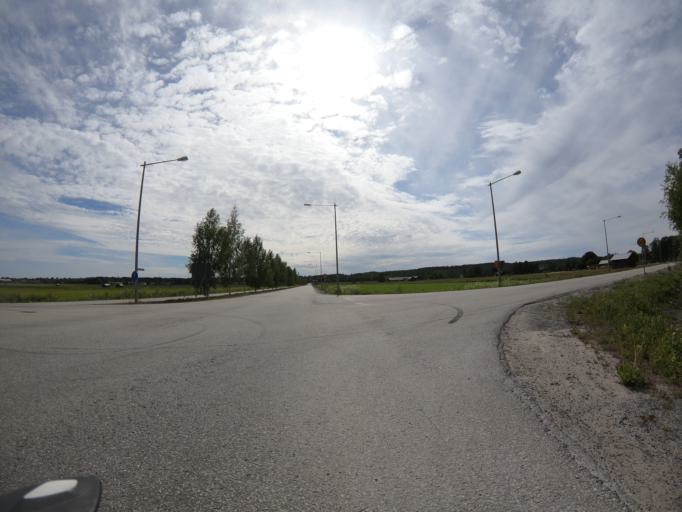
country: SE
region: Vaesterbotten
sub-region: Umea Kommun
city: Umea
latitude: 63.8225
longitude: 20.2395
